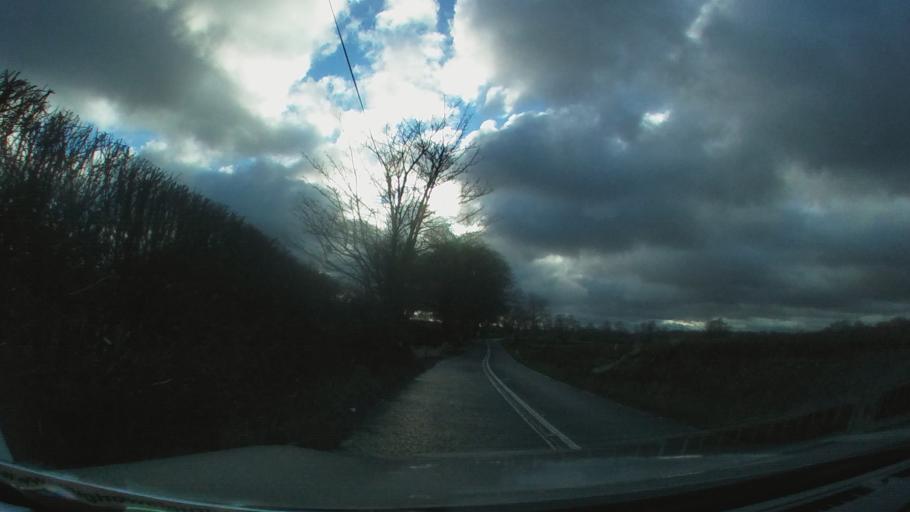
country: IE
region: Leinster
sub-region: Kilkenny
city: Thomastown
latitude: 52.5765
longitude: -7.1089
